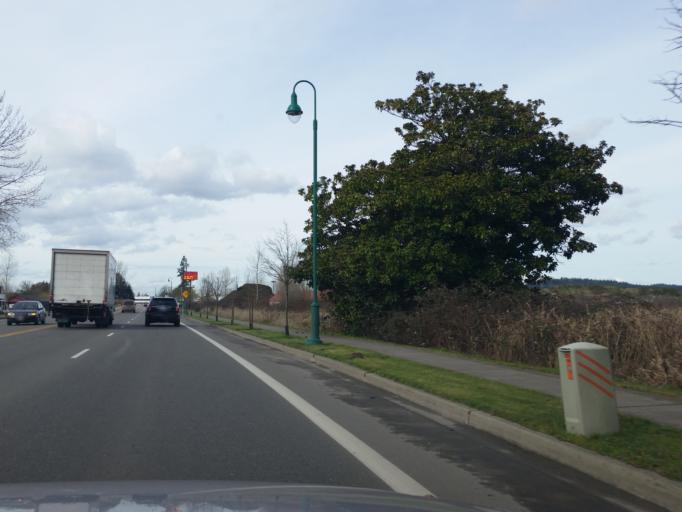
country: US
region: Washington
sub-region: Pierce County
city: Milton
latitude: 47.2236
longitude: -122.3262
